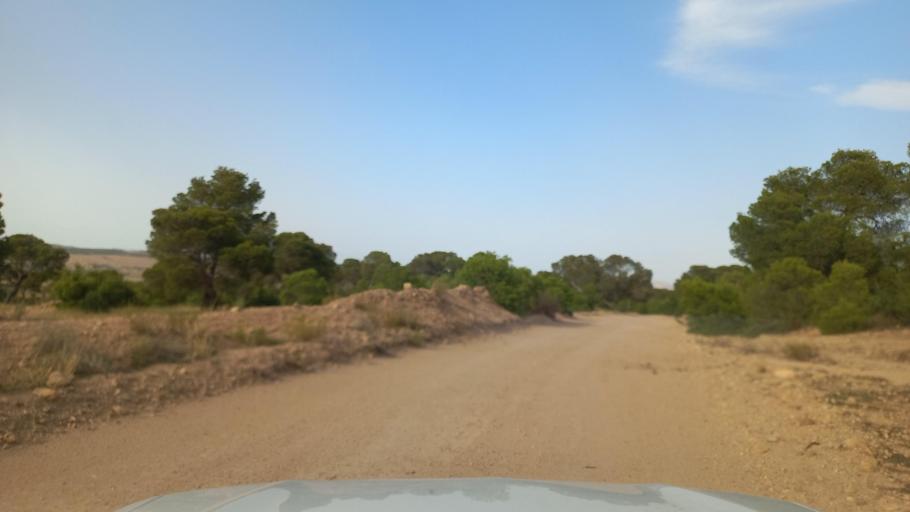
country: TN
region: Al Qasrayn
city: Kasserine
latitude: 35.3359
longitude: 8.8536
